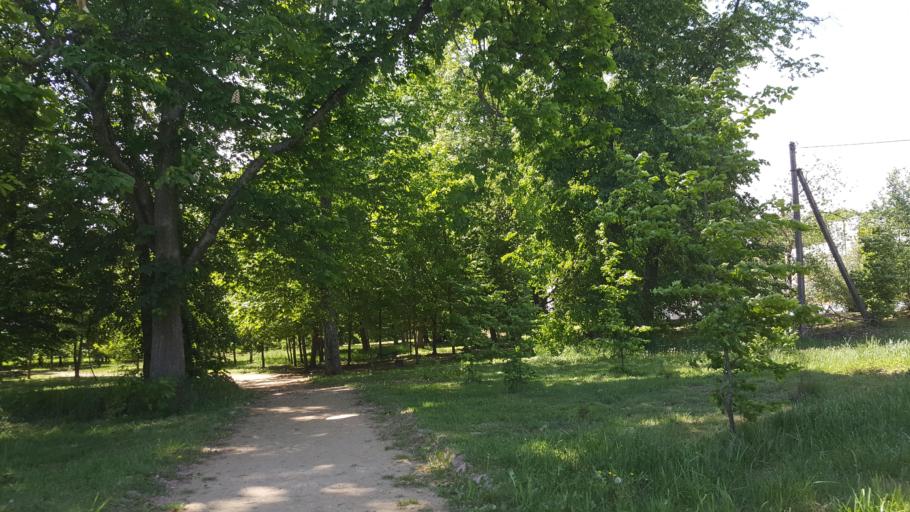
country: BY
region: Brest
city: Brest
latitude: 52.1558
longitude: 23.6397
